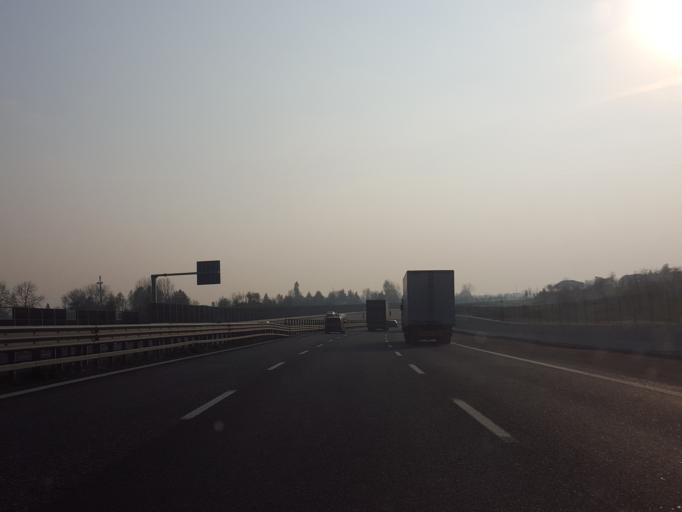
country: IT
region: Veneto
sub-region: Provincia di Venezia
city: Martellago
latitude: 45.5555
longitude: 12.1494
